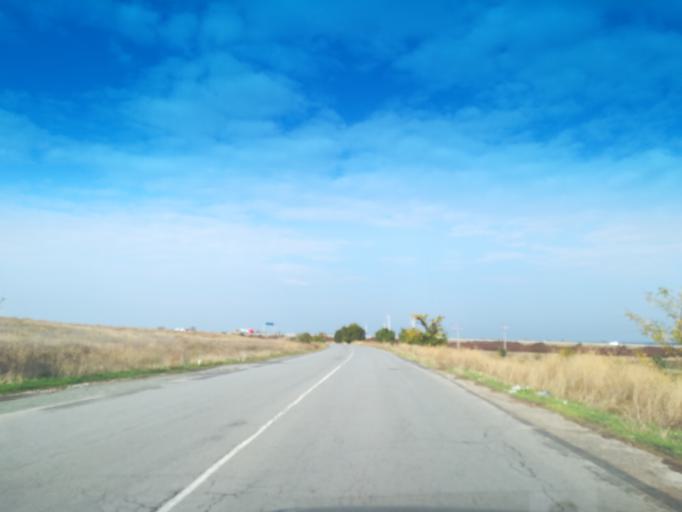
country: BG
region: Stara Zagora
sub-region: Obshtina Chirpan
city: Chirpan
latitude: 42.2062
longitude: 25.3071
